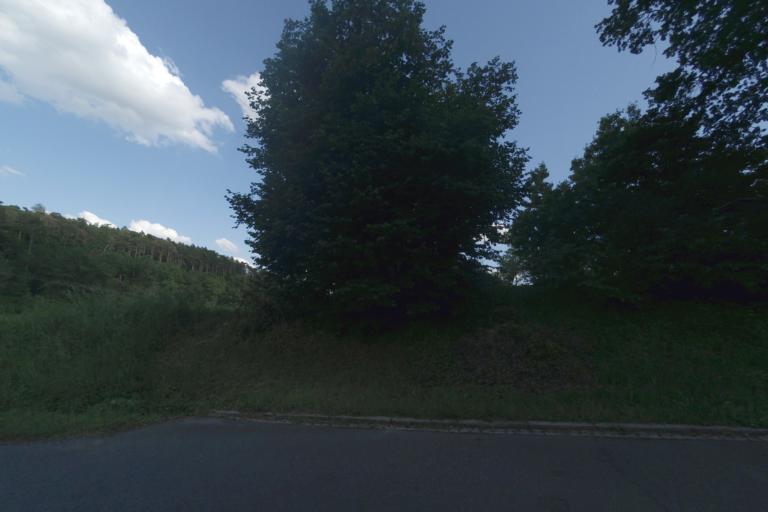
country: DE
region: Bavaria
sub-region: Regierungsbezirk Mittelfranken
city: Hagenbuchach
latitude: 49.5235
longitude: 10.7524
